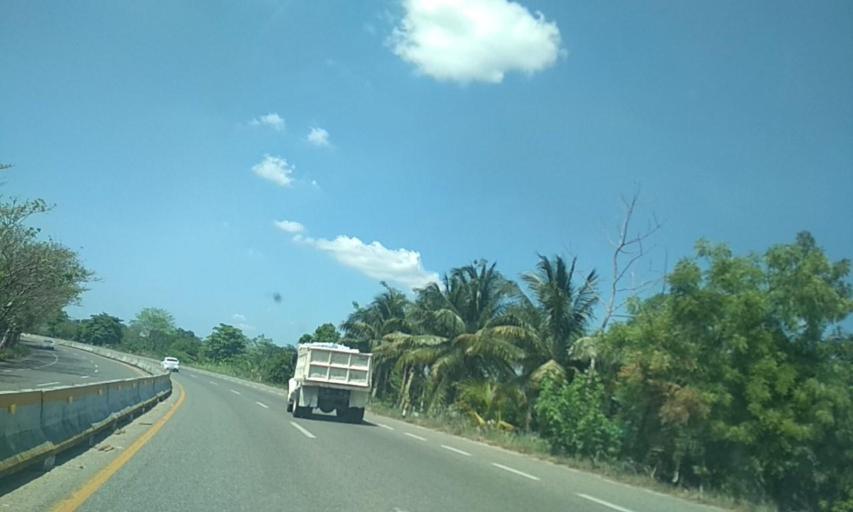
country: MX
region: Tabasco
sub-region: Huimanguillo
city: El Dorado
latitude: 17.8849
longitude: -93.3672
